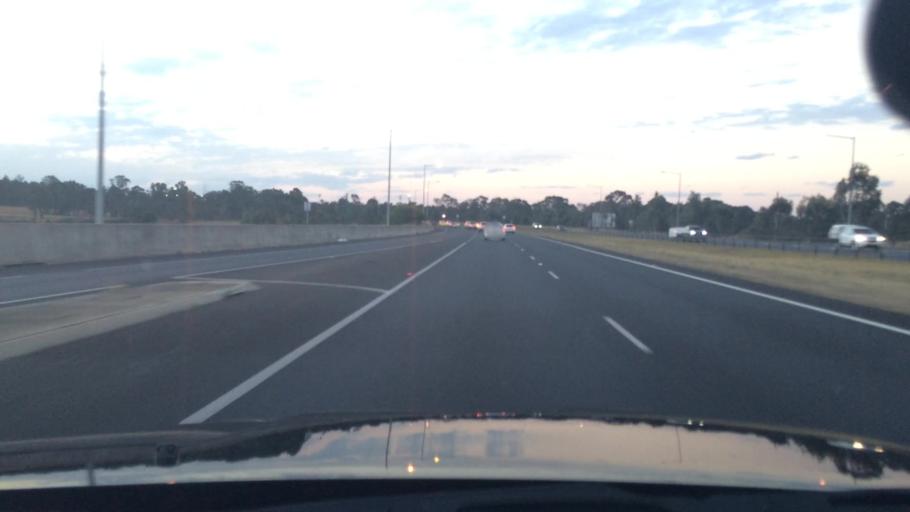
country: AU
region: New South Wales
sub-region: Blacktown
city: Doonside
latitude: -33.7856
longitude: 150.8575
